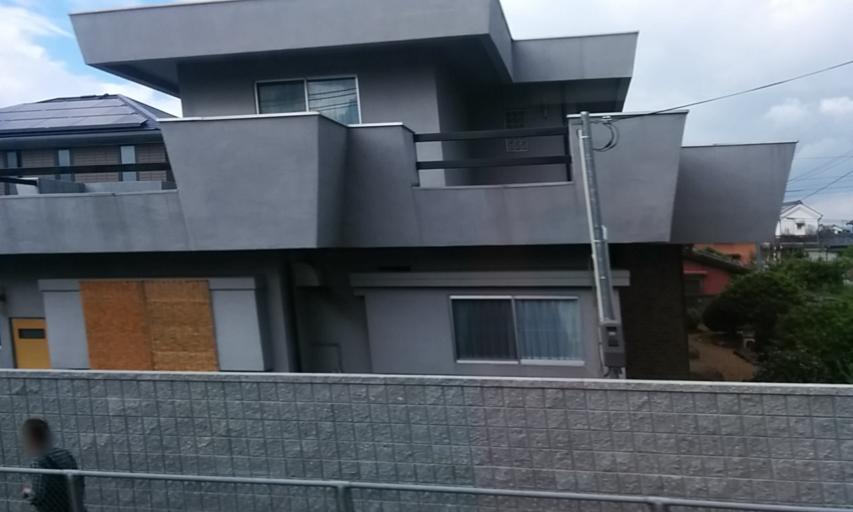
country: JP
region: Nara
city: Tawaramoto
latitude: 34.5410
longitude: 135.7941
